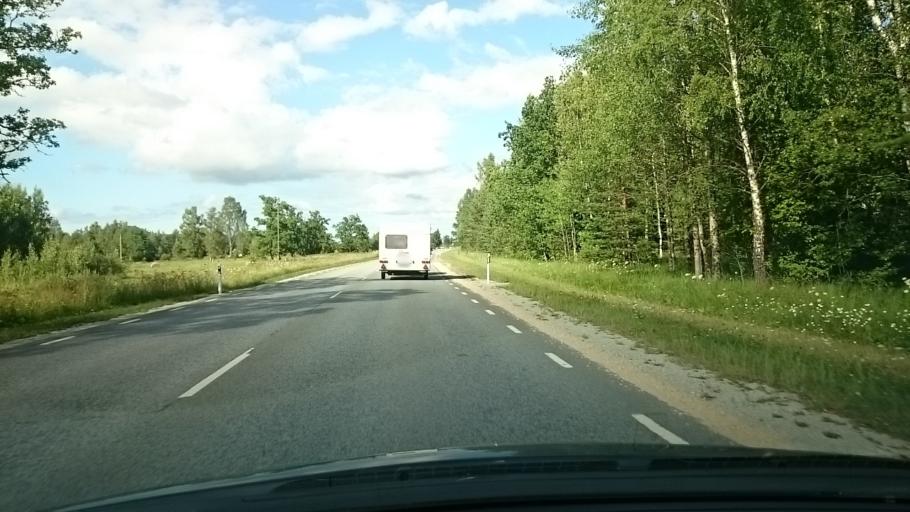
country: EE
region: Harju
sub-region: Keila linn
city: Keila
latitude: 59.2735
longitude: 24.2972
